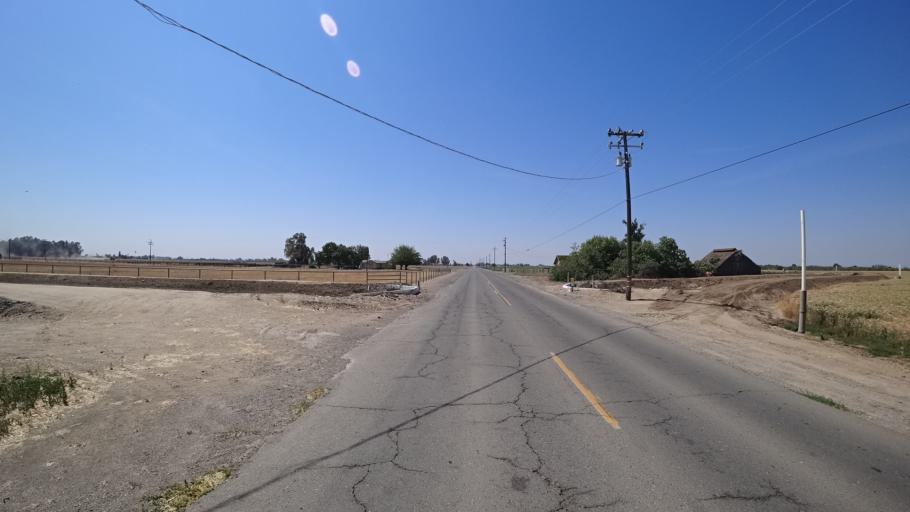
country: US
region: California
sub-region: Fresno County
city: Riverdale
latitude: 36.4101
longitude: -119.8512
